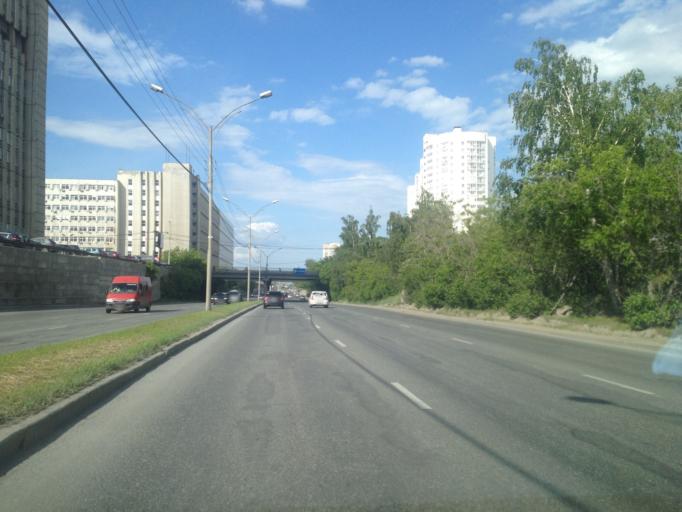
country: RU
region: Sverdlovsk
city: Sovkhoznyy
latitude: 56.8127
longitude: 60.5496
